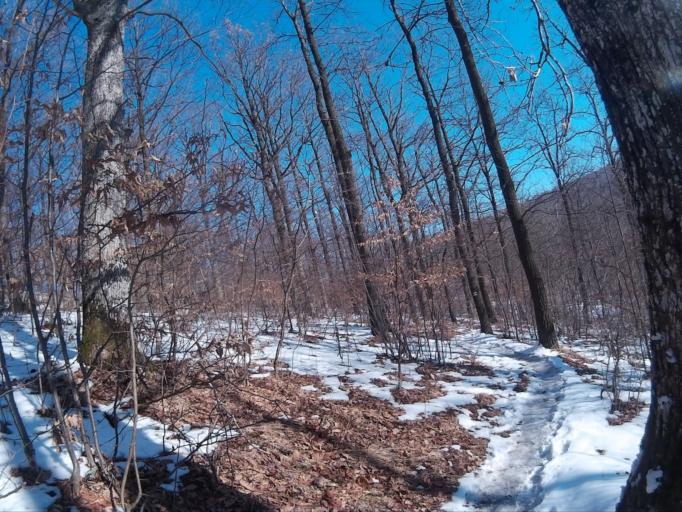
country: HU
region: Nograd
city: Batonyterenye
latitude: 47.9286
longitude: 19.8516
